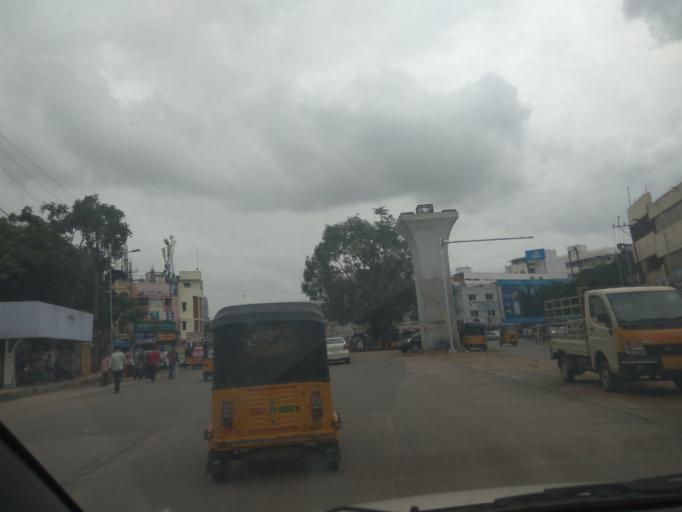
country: IN
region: Telangana
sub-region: Hyderabad
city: Hyderabad
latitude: 17.3959
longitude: 78.4908
